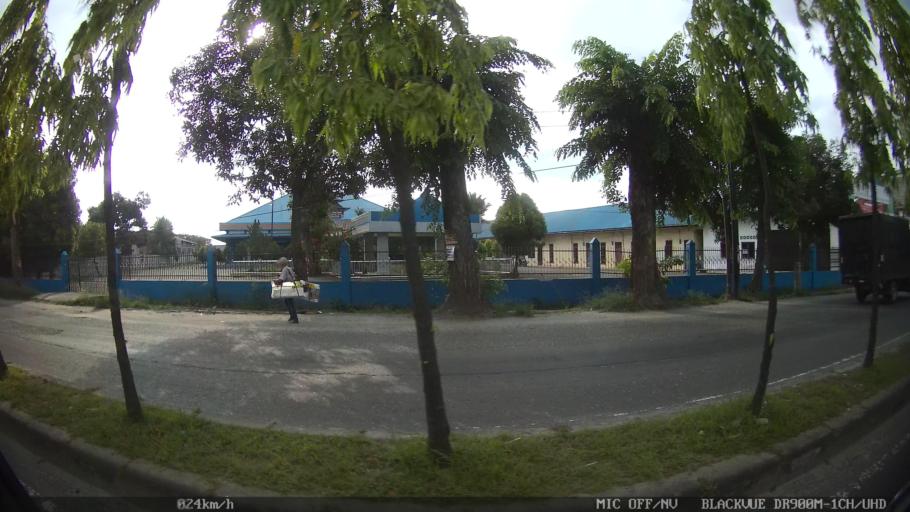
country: ID
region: North Sumatra
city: Sunggal
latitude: 3.5345
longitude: 98.6216
